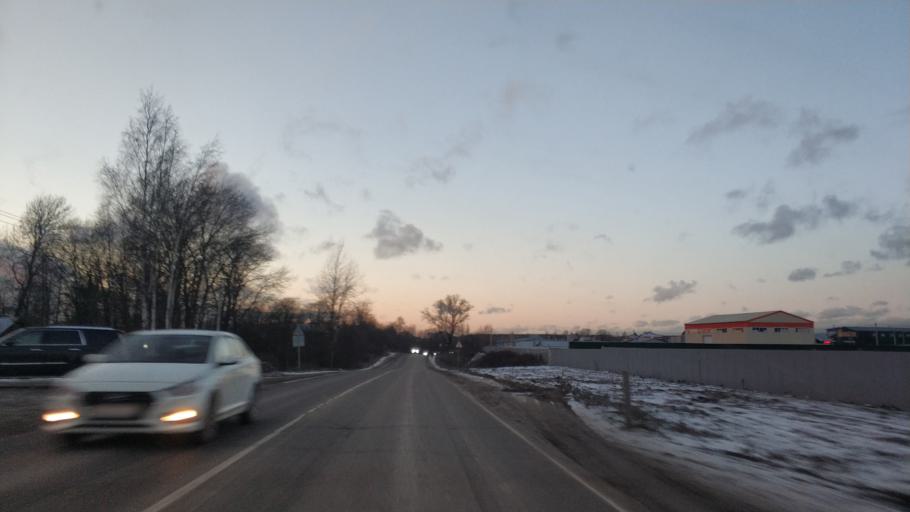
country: RU
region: St.-Petersburg
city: Pontonnyy
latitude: 59.8075
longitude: 30.6180
